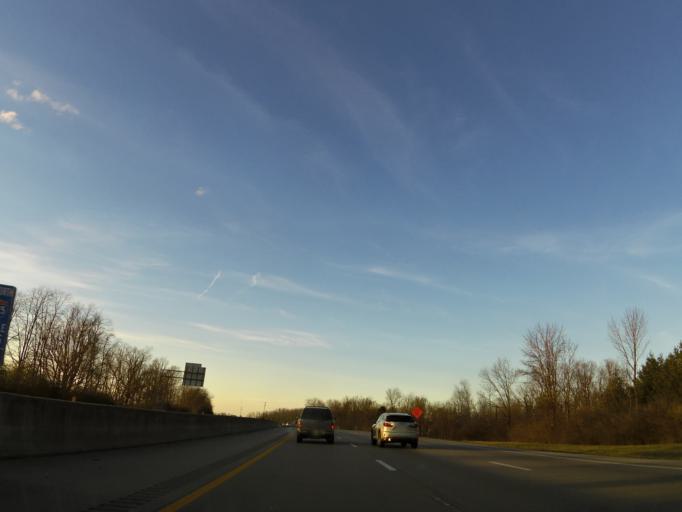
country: US
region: Kentucky
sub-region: Fayette County
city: Lexington
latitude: 37.9781
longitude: -84.3890
